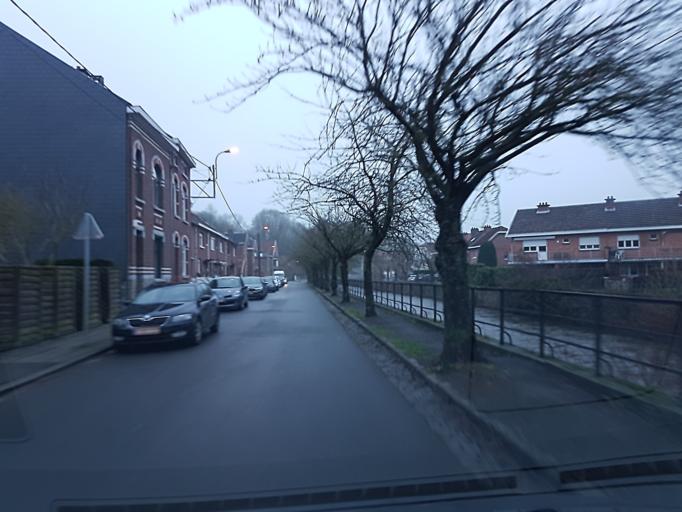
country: BE
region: Wallonia
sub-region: Province de Liege
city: Theux
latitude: 50.5371
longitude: 5.8120
